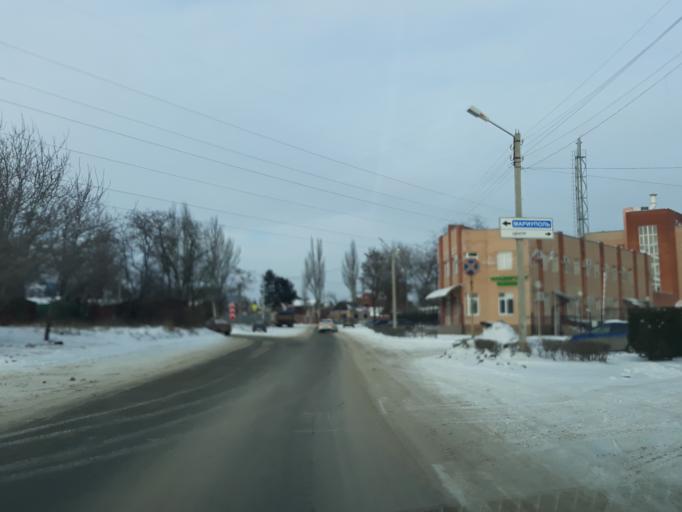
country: RU
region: Rostov
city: Taganrog
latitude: 47.2252
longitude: 38.8583
